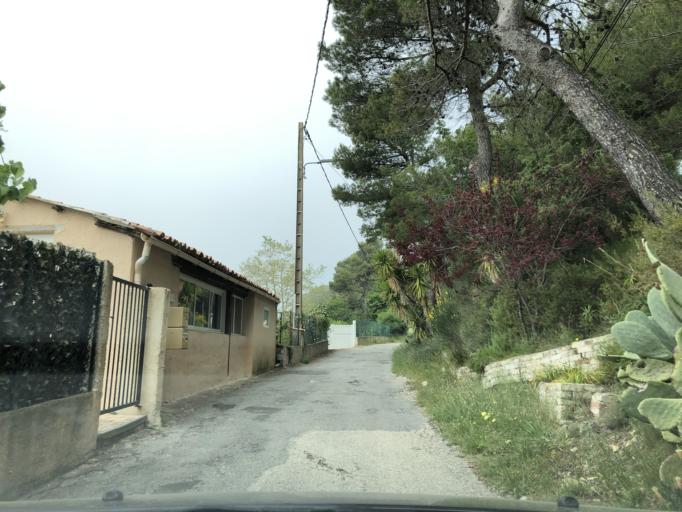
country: FR
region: Provence-Alpes-Cote d'Azur
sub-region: Departement des Alpes-Maritimes
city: Eze
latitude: 43.7359
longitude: 7.3445
